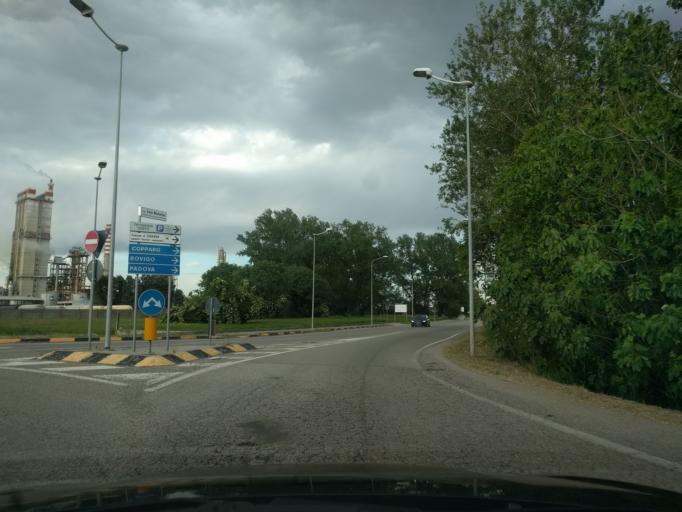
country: IT
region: Emilia-Romagna
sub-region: Provincia di Ferrara
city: Ferrara
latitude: 44.8514
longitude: 11.5878
